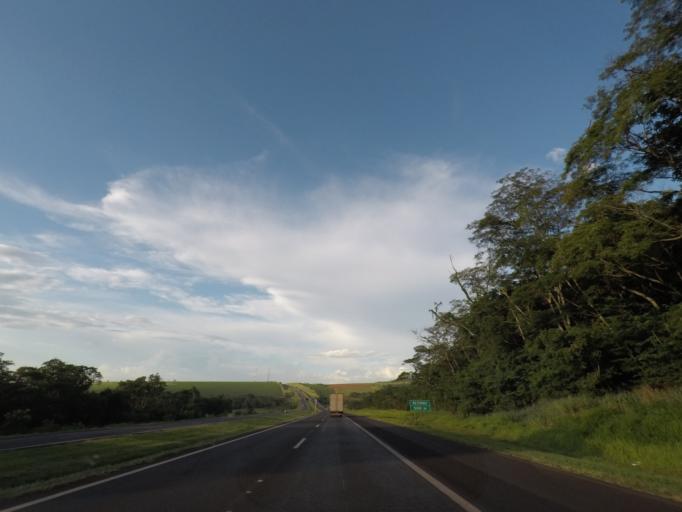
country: BR
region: Sao Paulo
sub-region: Ituverava
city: Ituverava
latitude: -20.2886
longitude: -47.7976
